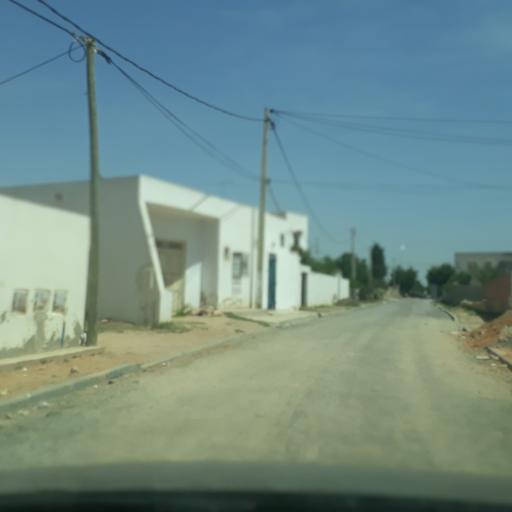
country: TN
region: Safaqis
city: Al Qarmadah
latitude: 34.8265
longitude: 10.7815
